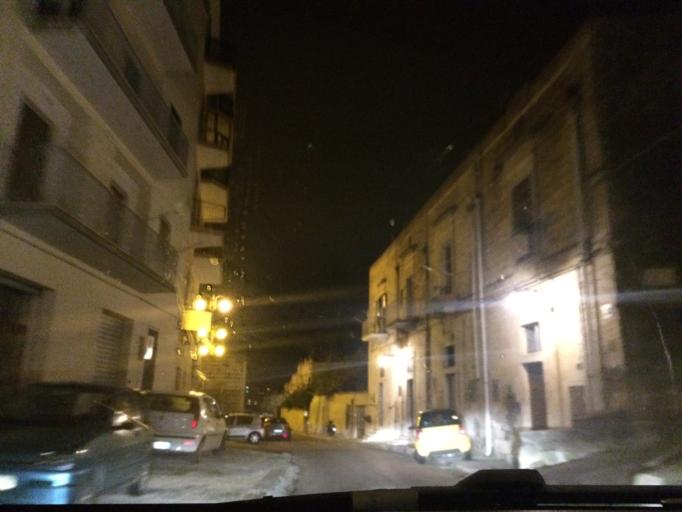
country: IT
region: Basilicate
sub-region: Provincia di Matera
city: Matera
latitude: 40.6590
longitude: 16.6155
